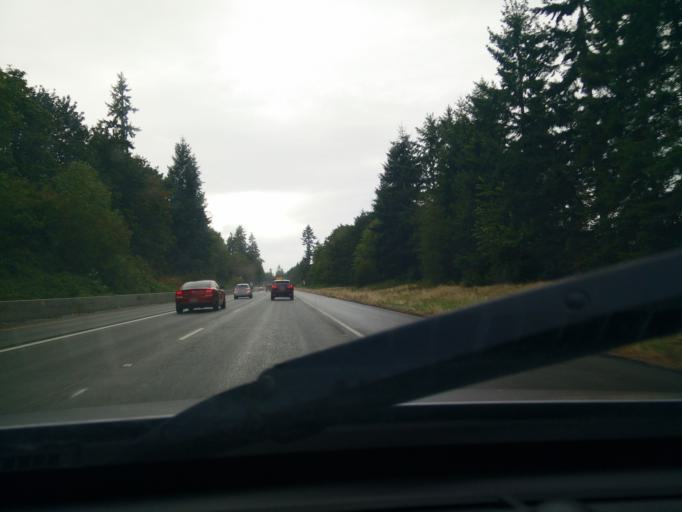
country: US
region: Washington
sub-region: Snohomish County
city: Martha Lake
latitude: 47.8066
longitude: -122.2272
